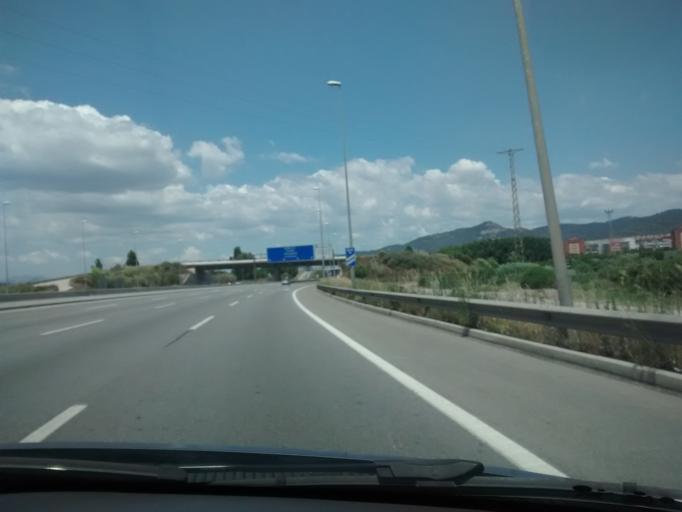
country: ES
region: Catalonia
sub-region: Provincia de Barcelona
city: Sant Joan Despi
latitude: 41.3578
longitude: 2.0516
